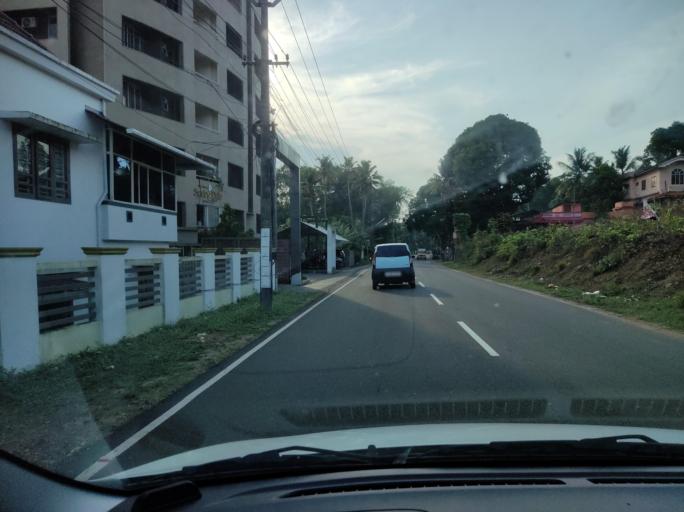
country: IN
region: Kerala
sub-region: Kottayam
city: Kottayam
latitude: 9.6441
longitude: 76.5309
